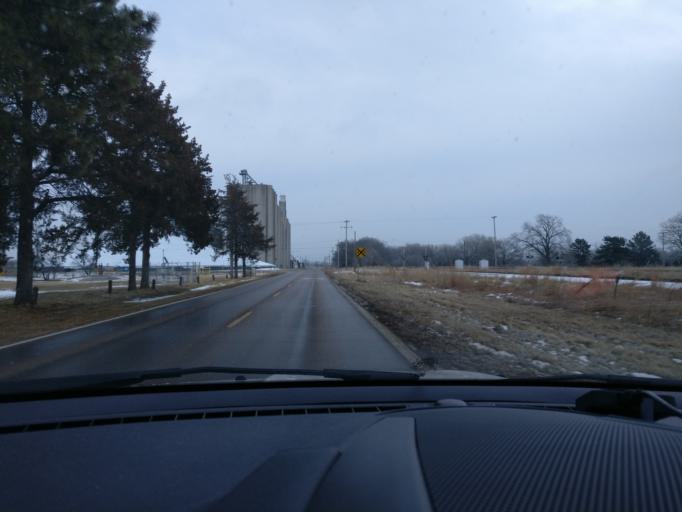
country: US
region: Nebraska
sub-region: Dodge County
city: Fremont
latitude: 41.4479
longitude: -96.5602
